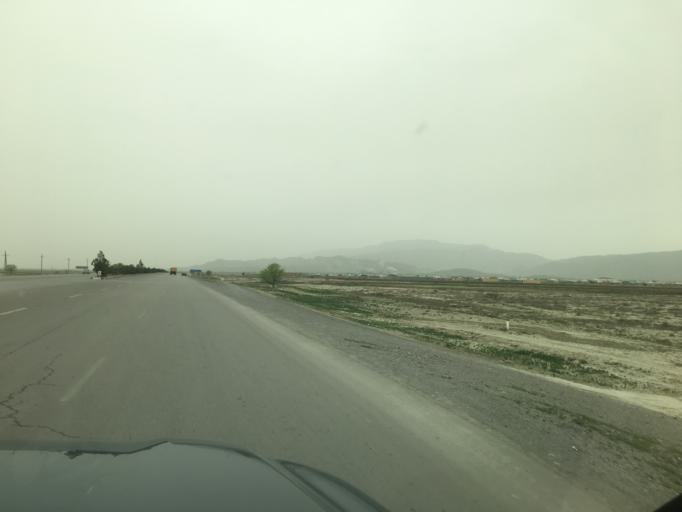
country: TM
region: Ahal
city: Baharly
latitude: 38.3096
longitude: 57.6152
